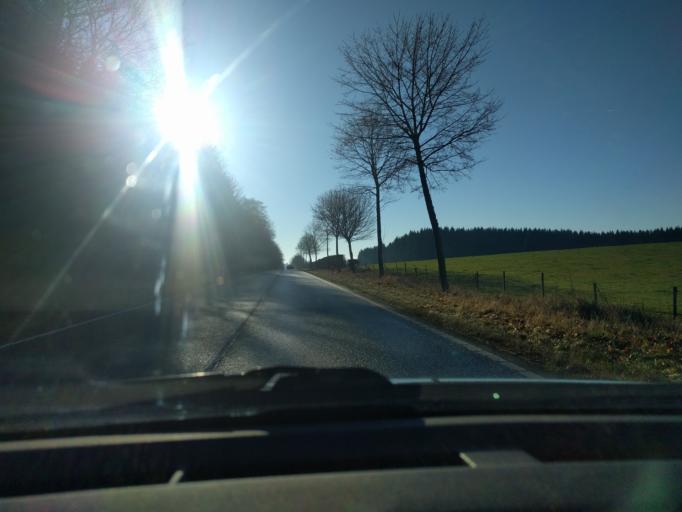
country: LU
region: Diekirch
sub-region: Canton de Clervaux
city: Troisvierges
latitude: 50.1784
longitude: 6.0249
